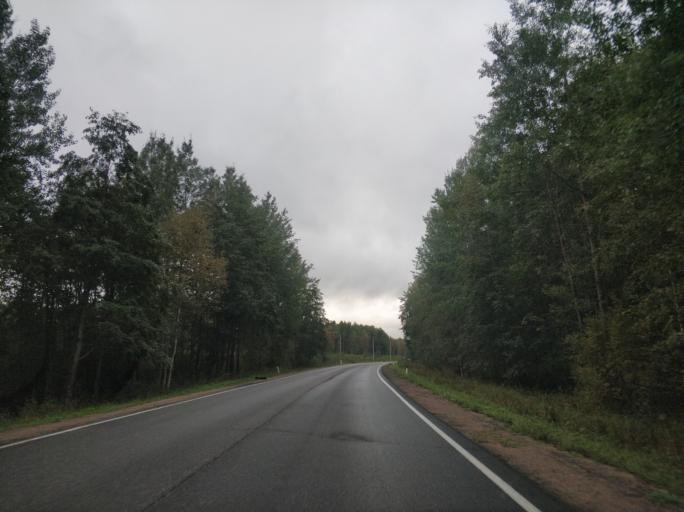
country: RU
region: Leningrad
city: Borisova Griva
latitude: 60.1154
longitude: 30.9637
